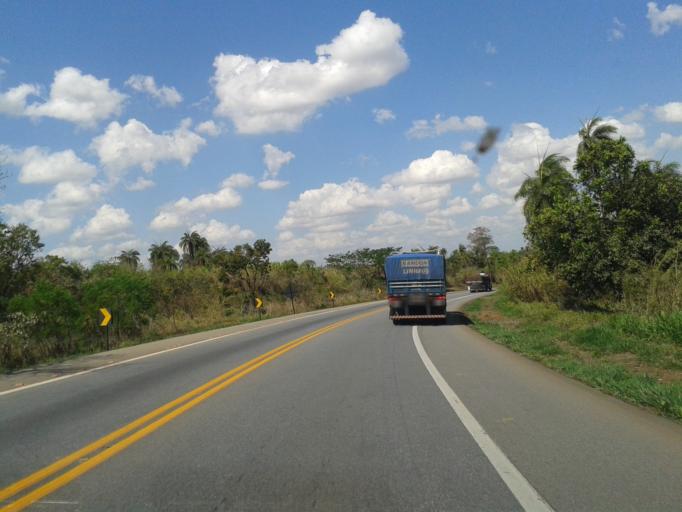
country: BR
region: Minas Gerais
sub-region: Luz
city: Luz
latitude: -19.7397
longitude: -45.8492
